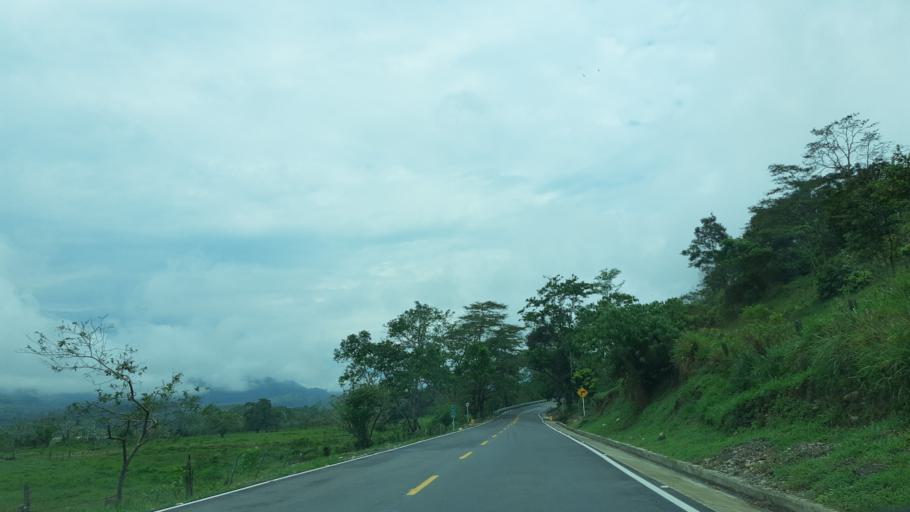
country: CO
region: Casanare
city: Sabanalarga
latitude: 4.7777
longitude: -73.0496
